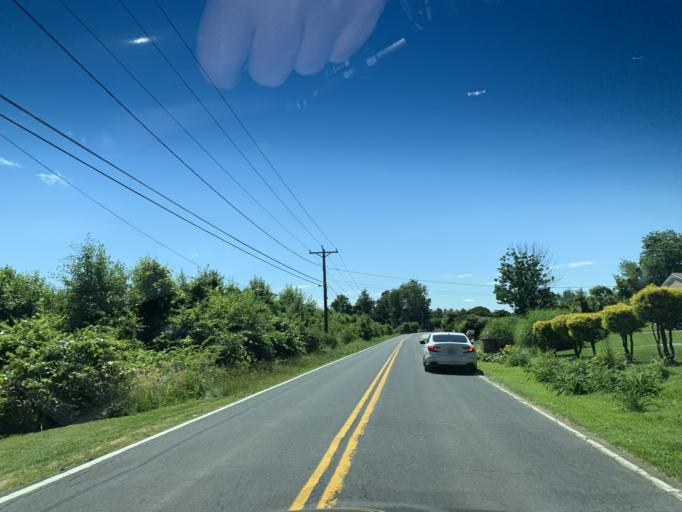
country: US
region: Maryland
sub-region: Harford County
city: Aberdeen
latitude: 39.5536
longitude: -76.1442
